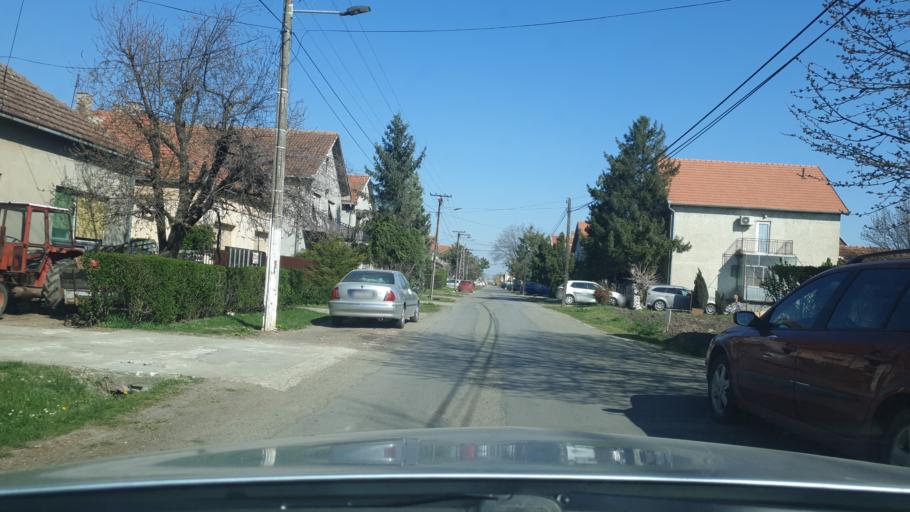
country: RS
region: Autonomna Pokrajina Vojvodina
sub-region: Sremski Okrug
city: Stara Pazova
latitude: 44.9911
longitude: 20.1426
